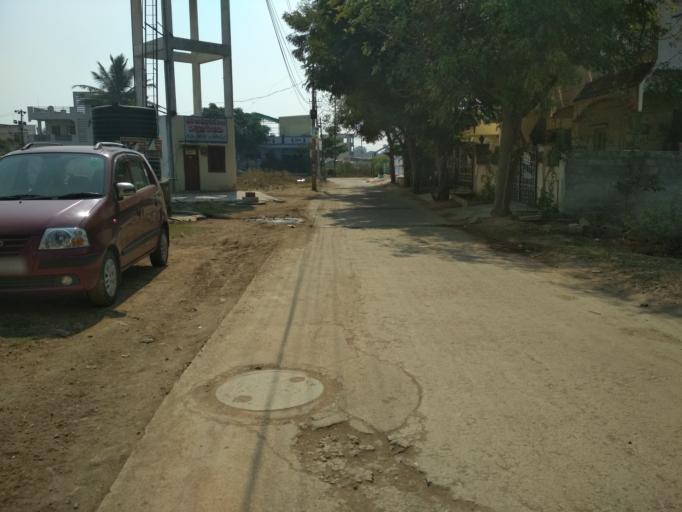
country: IN
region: Telangana
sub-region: Rangareddi
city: Uppal Kalan
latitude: 17.4210
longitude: 78.5764
